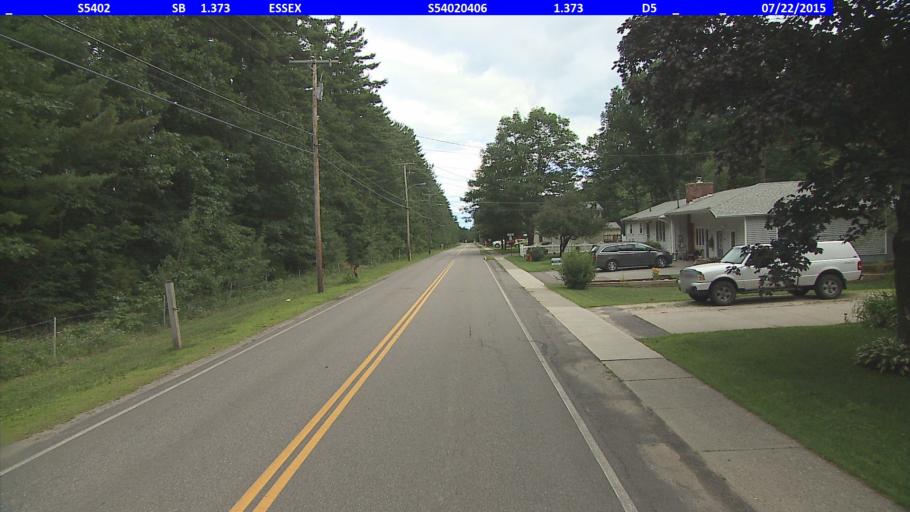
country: US
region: Vermont
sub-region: Chittenden County
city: Jericho
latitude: 44.4980
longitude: -73.0494
